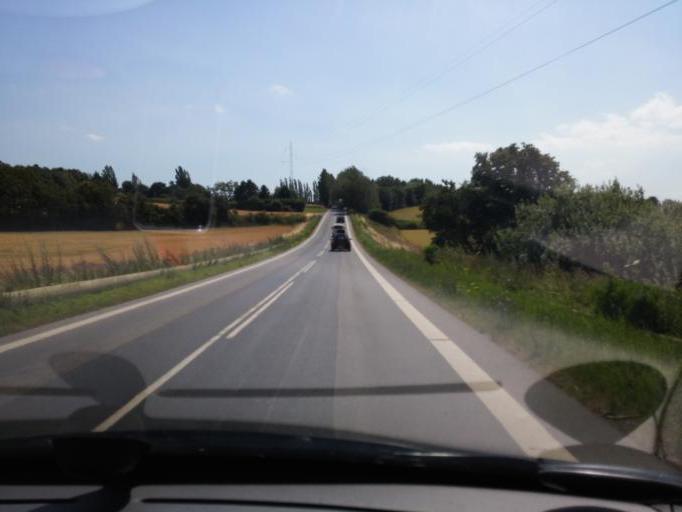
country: DK
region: South Denmark
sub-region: Langeland Kommune
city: Rudkobing
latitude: 54.8518
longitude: 10.7165
